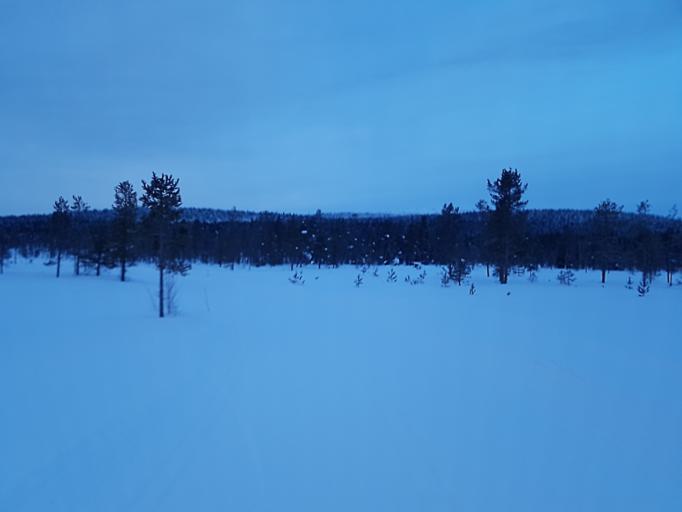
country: FI
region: Lapland
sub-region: Tunturi-Lappi
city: Kolari
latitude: 67.6186
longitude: 24.1317
